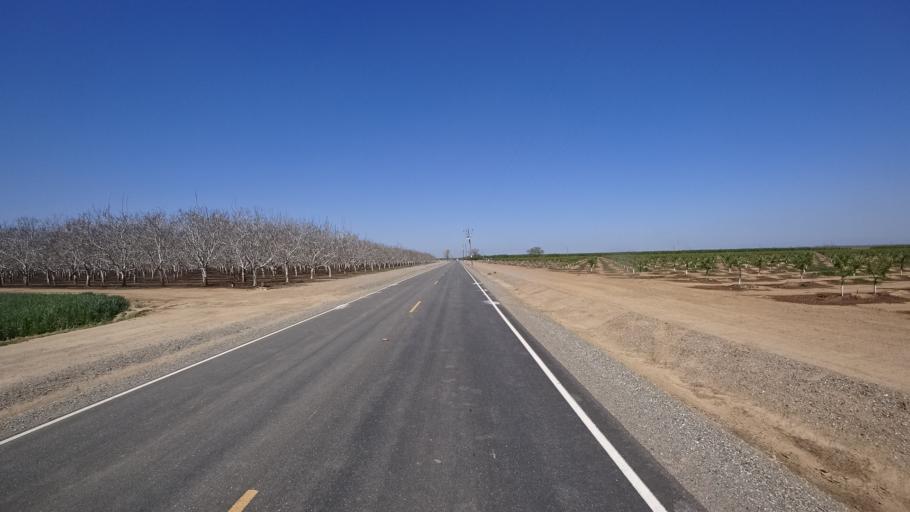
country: US
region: California
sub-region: Glenn County
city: Willows
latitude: 39.6080
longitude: -122.1376
